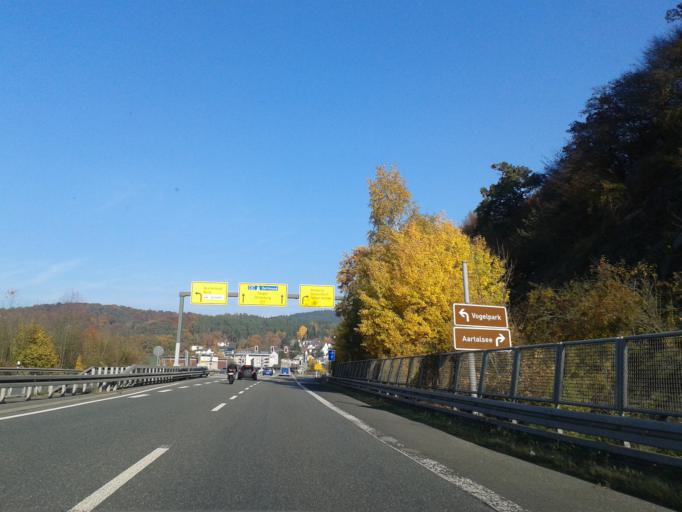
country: DE
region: Hesse
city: Herborn
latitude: 50.6972
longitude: 8.3090
